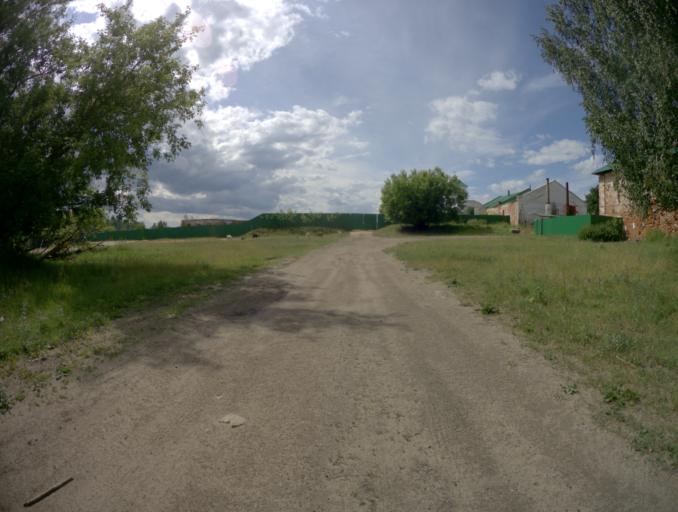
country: RU
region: Nizjnij Novgorod
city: Frolishchi
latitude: 56.4213
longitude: 42.6442
